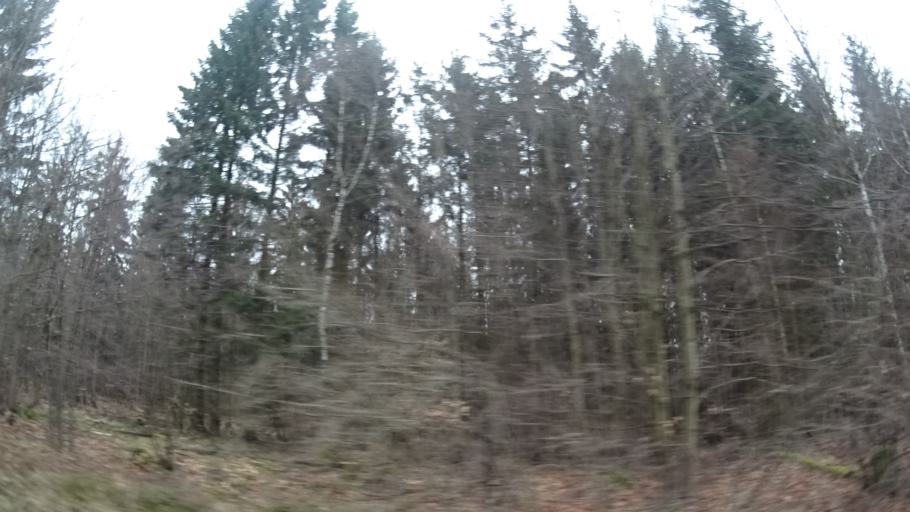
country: DE
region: Rheinland-Pfalz
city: Ippenschied
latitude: 49.8969
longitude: 7.6170
